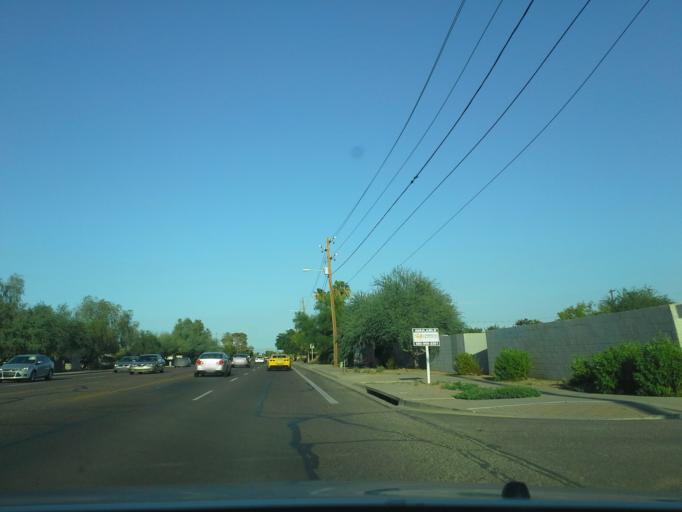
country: US
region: Arizona
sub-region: Maricopa County
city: Guadalupe
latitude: 33.3933
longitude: -112.0259
